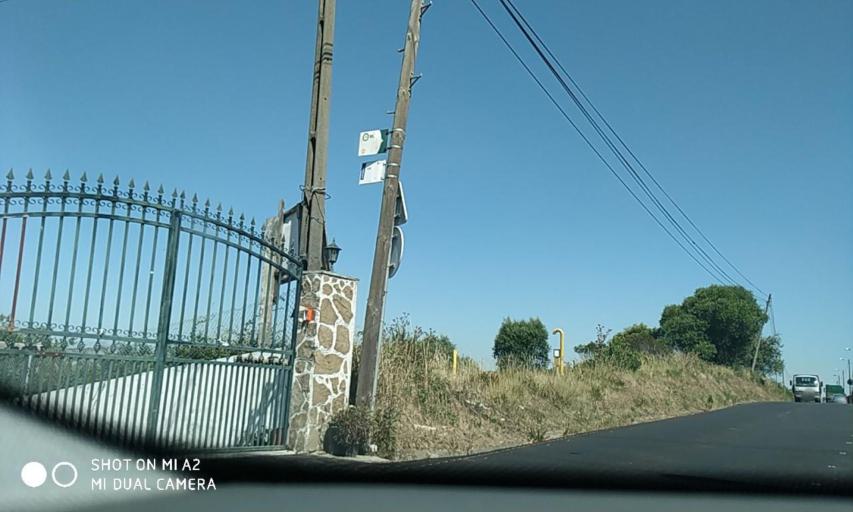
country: PT
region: Lisbon
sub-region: Sintra
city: Almargem
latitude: 38.8251
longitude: -9.2631
